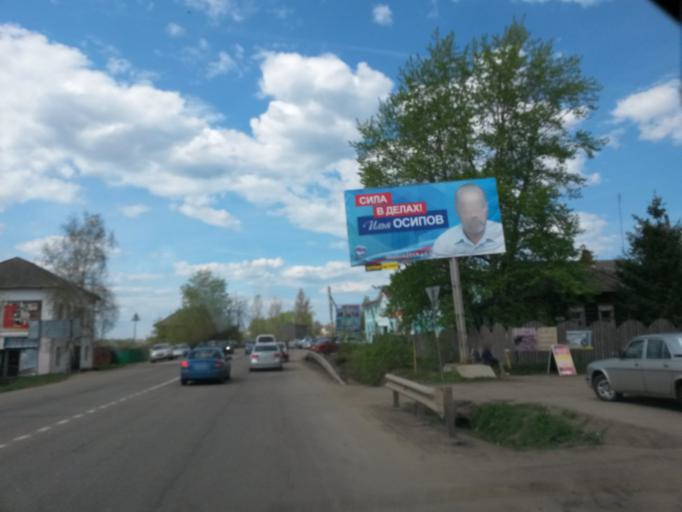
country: RU
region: Jaroslavl
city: Bol'shoye Selo
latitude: 57.7215
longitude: 38.9408
